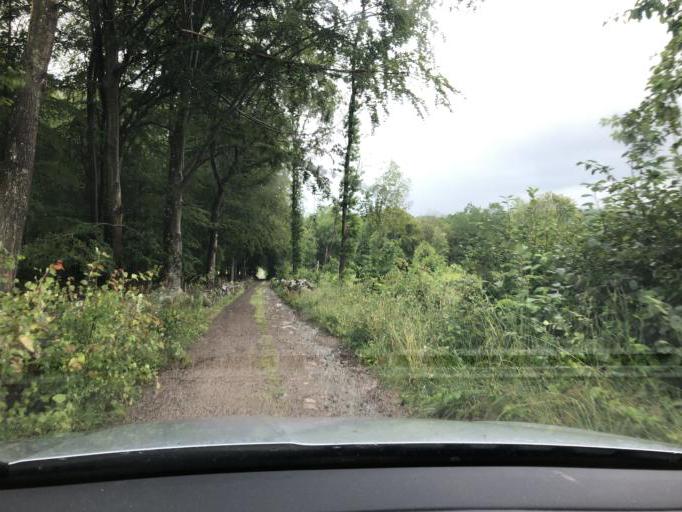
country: SE
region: Blekinge
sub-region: Solvesborgs Kommun
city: Soelvesborg
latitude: 56.1294
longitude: 14.5982
